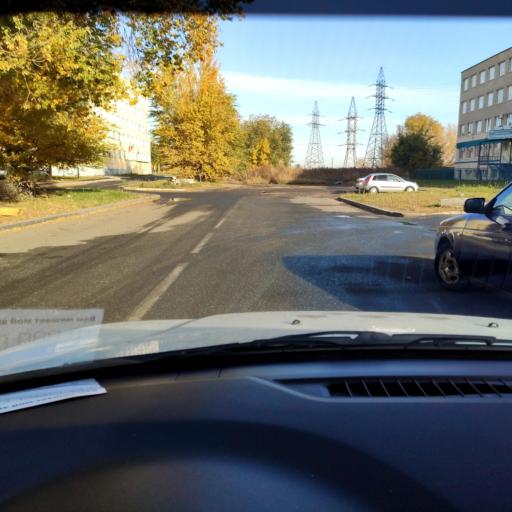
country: RU
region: Samara
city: Tol'yatti
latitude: 53.5405
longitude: 49.4089
